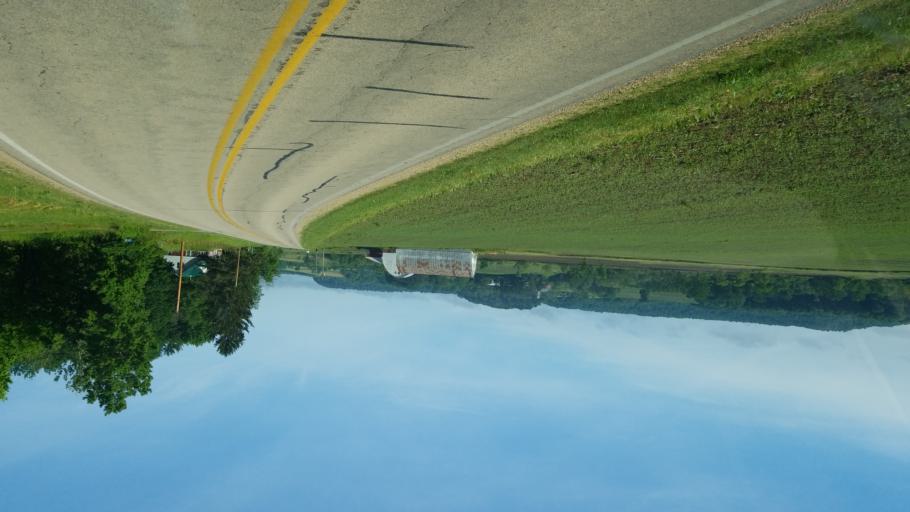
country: US
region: Wisconsin
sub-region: Juneau County
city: Elroy
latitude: 43.6356
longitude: -90.2240
